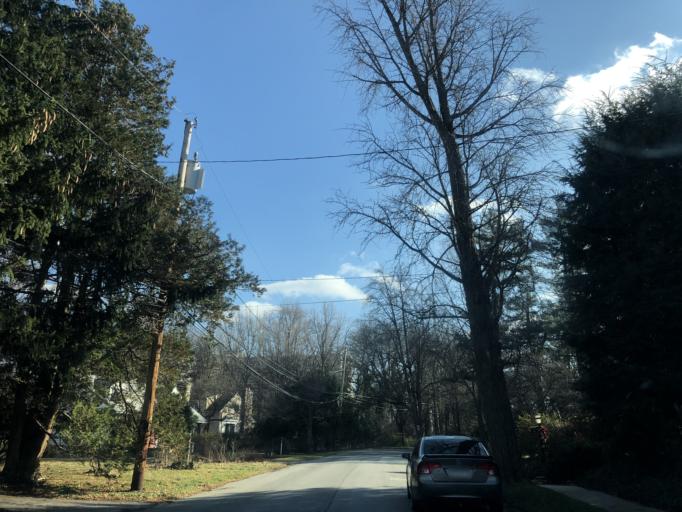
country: US
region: Pennsylvania
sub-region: Montgomery County
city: Bala-Cynwyd
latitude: 40.0064
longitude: -75.2262
